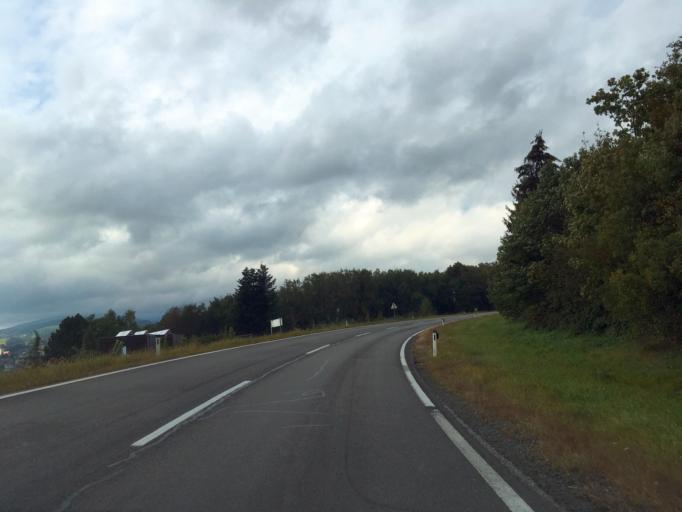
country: AT
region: Styria
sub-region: Politischer Bezirk Hartberg-Fuerstenfeld
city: Pinggau
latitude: 47.4364
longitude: 16.0802
